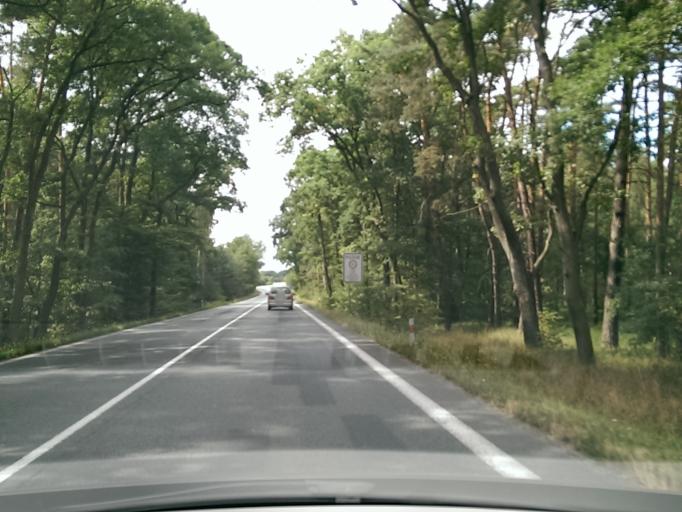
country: CZ
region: Central Bohemia
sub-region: Okres Nymburk
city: Podebrady
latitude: 50.1119
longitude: 15.1320
